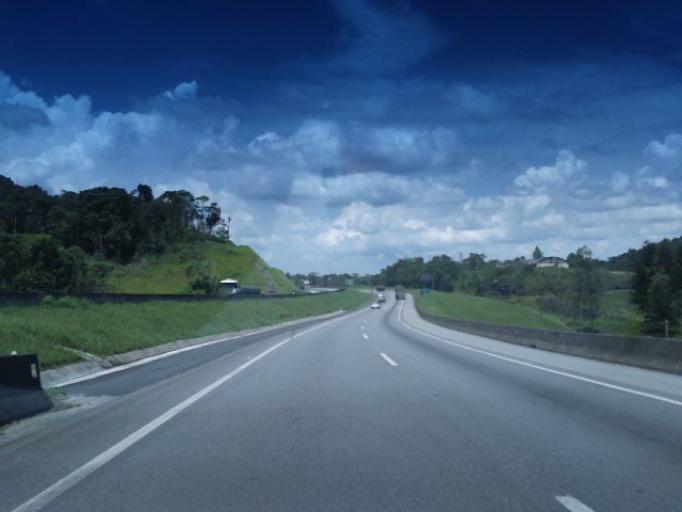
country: BR
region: Sao Paulo
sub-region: Juquitiba
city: Juquitiba
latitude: -23.9750
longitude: -47.1405
